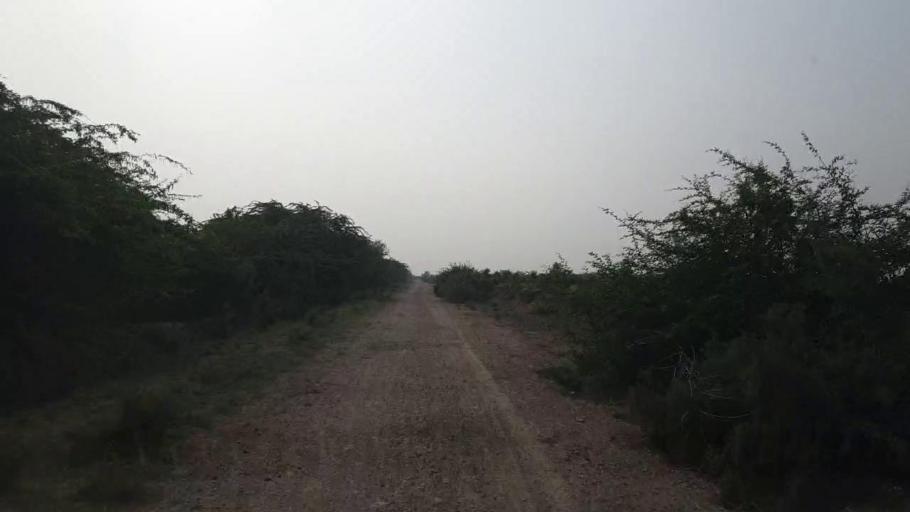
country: PK
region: Sindh
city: Mirpur Batoro
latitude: 24.6226
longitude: 68.4032
